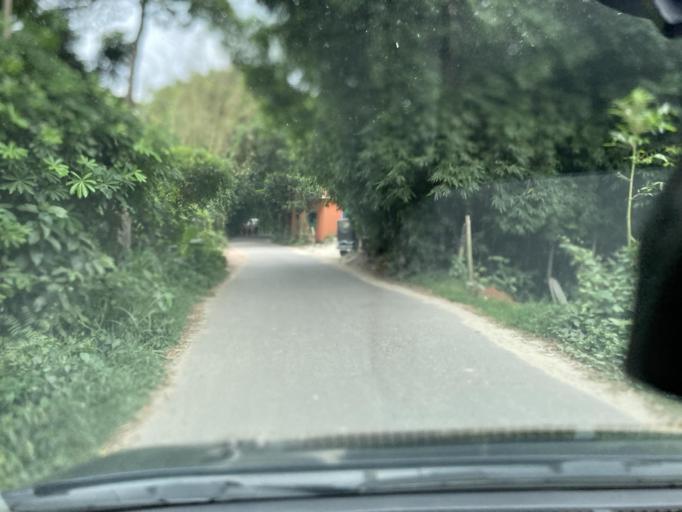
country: BD
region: Dhaka
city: Dohar
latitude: 23.7944
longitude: 90.0523
